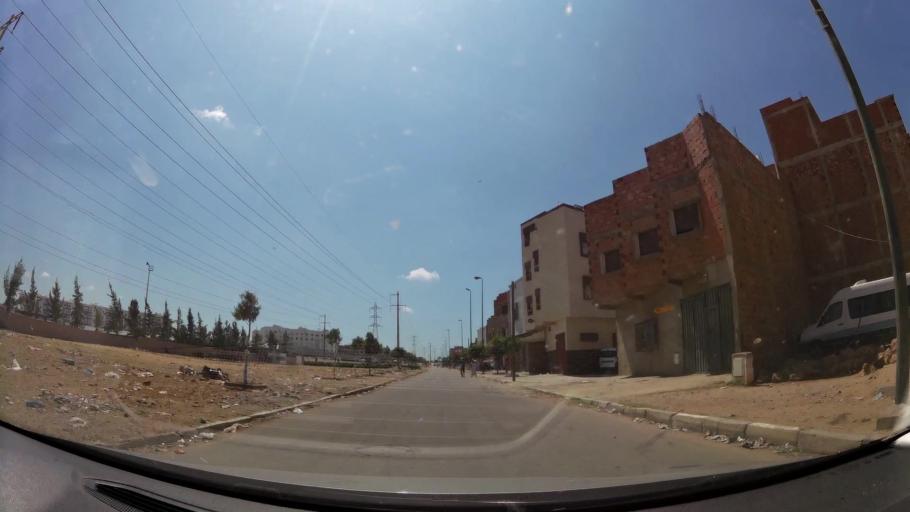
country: MA
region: Gharb-Chrarda-Beni Hssen
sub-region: Kenitra Province
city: Kenitra
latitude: 34.2379
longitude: -6.5410
